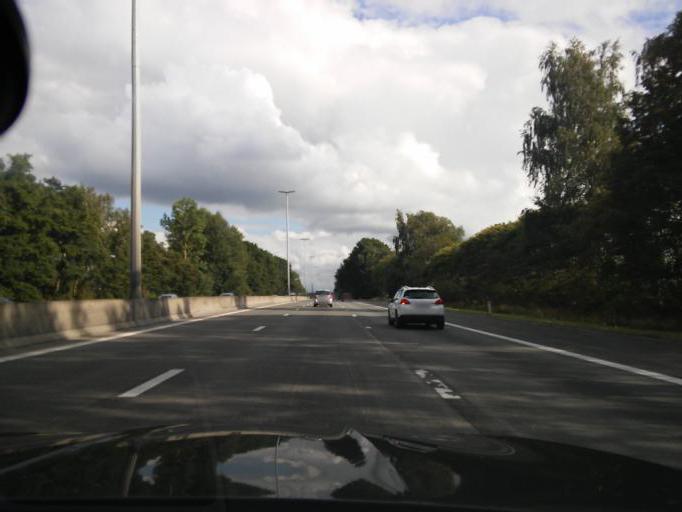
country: BE
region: Flanders
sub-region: Provincie Oost-Vlaanderen
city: Denderleeuw
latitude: 50.9031
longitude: 4.0871
